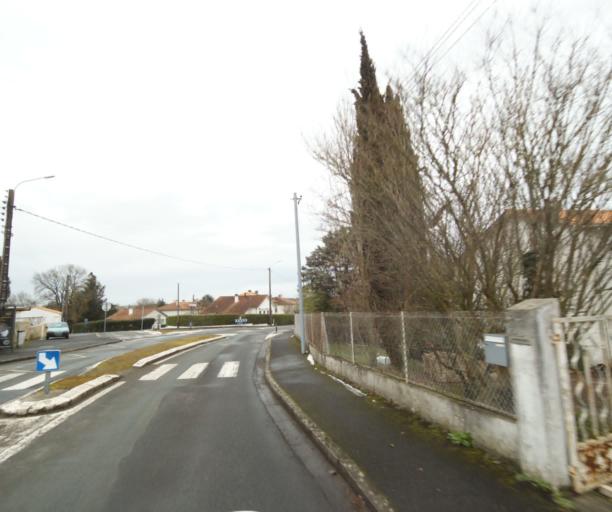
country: FR
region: Poitou-Charentes
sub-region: Departement des Deux-Sevres
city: Niort
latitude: 46.3387
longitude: -0.4560
